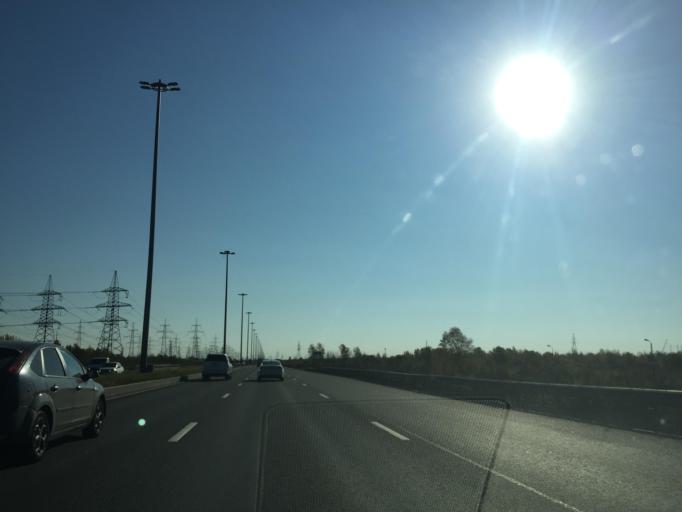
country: RU
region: St.-Petersburg
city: Petro-Slavyanka
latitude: 59.7642
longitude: 30.5056
